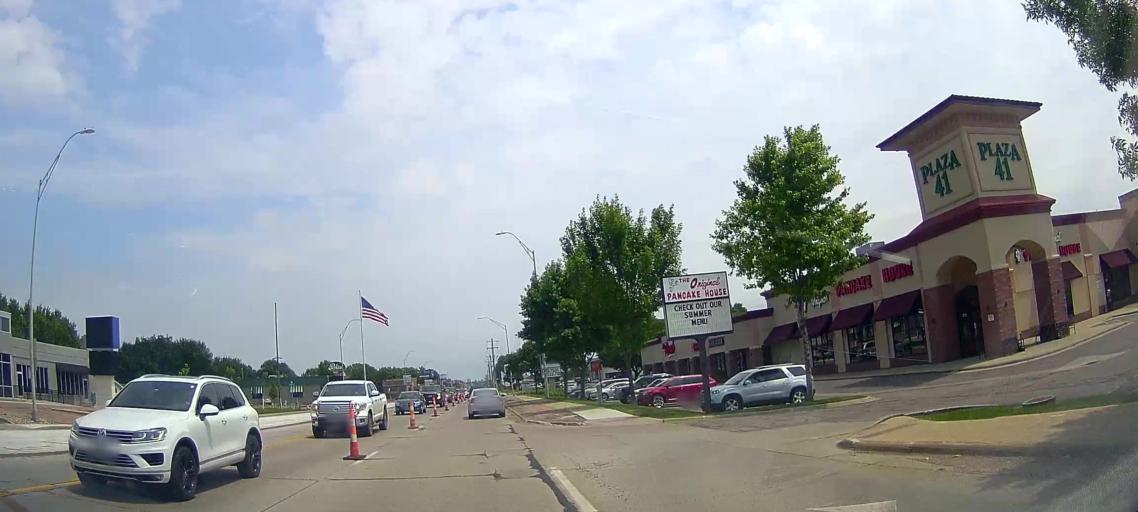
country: US
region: South Dakota
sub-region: Minnehaha County
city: Sioux Falls
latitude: 43.5148
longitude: -96.7595
